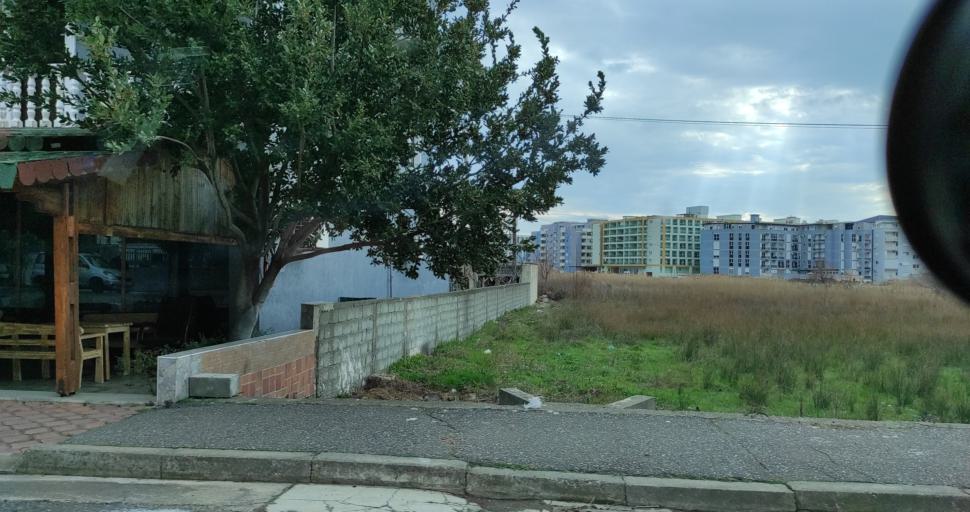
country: AL
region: Lezhe
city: Shengjin
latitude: 41.8086
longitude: 19.6033
